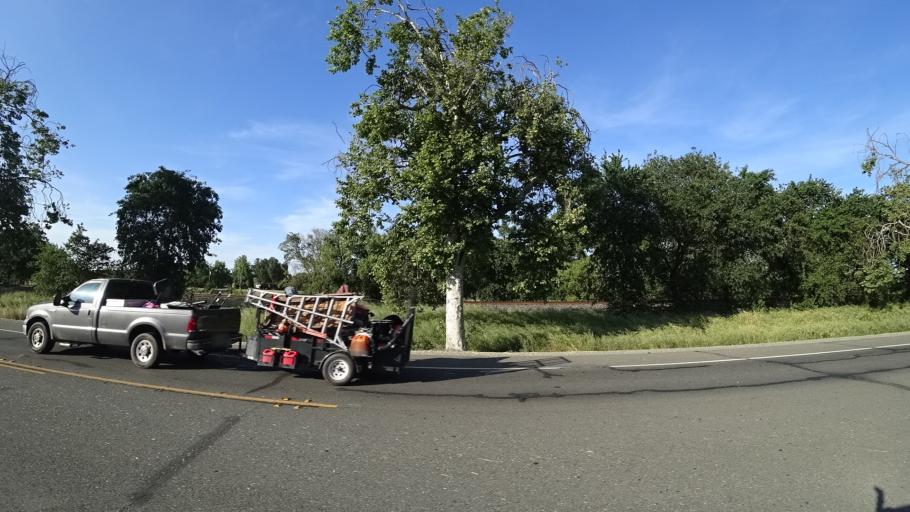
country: US
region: California
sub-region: Yuba County
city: Wheatland
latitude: 39.0152
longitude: -121.4327
